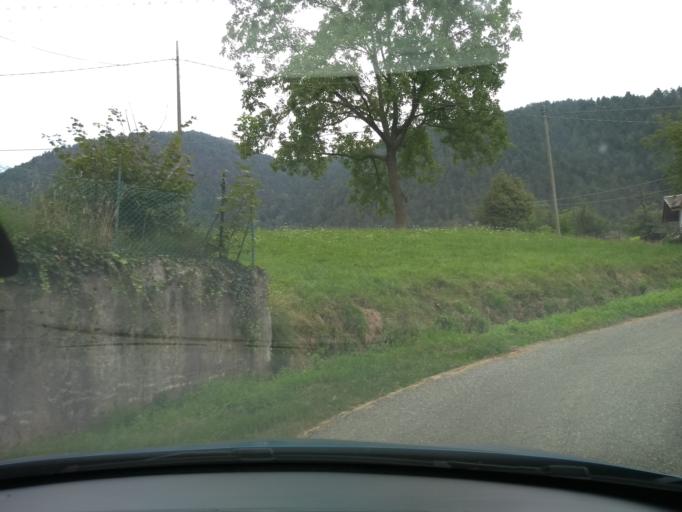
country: IT
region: Piedmont
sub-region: Provincia di Torino
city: La Villa
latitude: 45.2348
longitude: 7.4247
